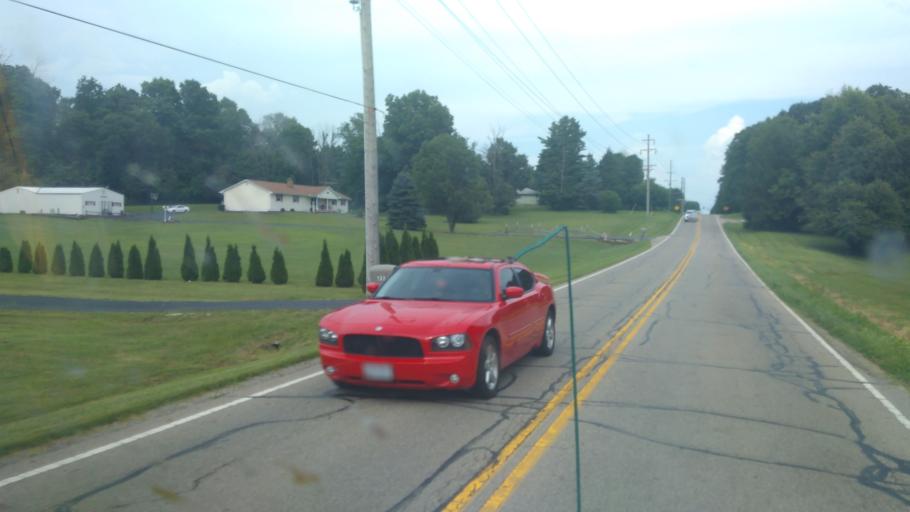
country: US
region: Ohio
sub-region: Fairfield County
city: Lancaster
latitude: 39.7680
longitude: -82.5822
